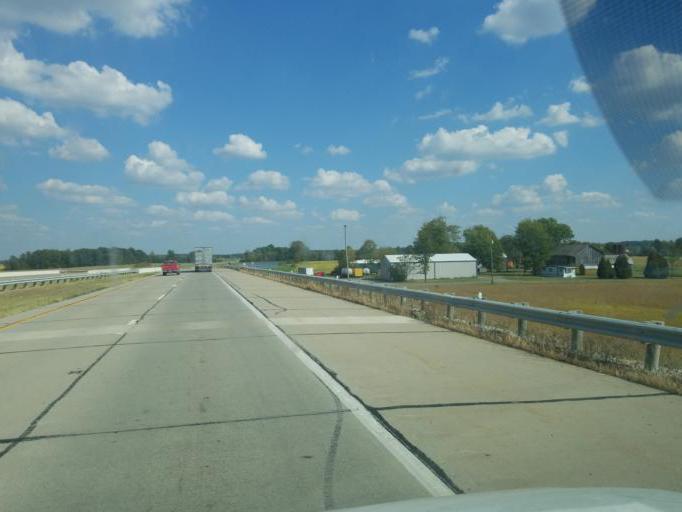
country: US
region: Ohio
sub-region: Allen County
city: Bluffton
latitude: 40.8270
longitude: -83.9008
